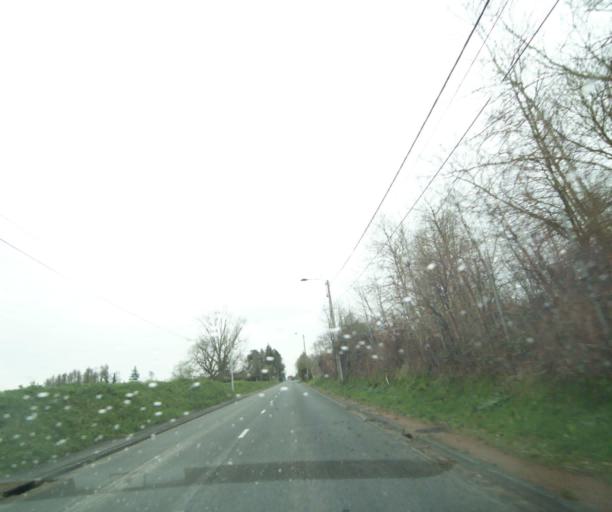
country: FR
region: Nord-Pas-de-Calais
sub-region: Departement du Nord
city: Quievrechain
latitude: 50.3856
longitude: 3.6595
